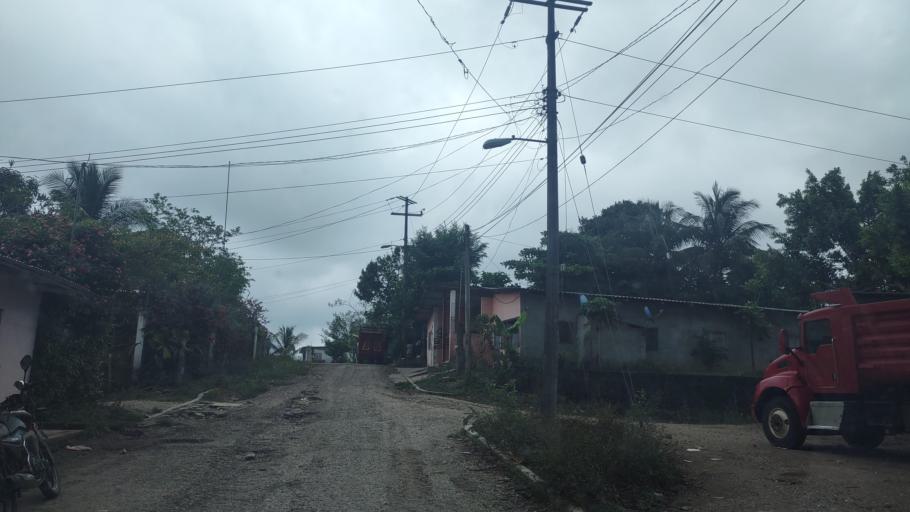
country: MX
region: Veracruz
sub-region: Uxpanapa
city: Poblado 10
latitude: 17.4952
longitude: -94.1614
